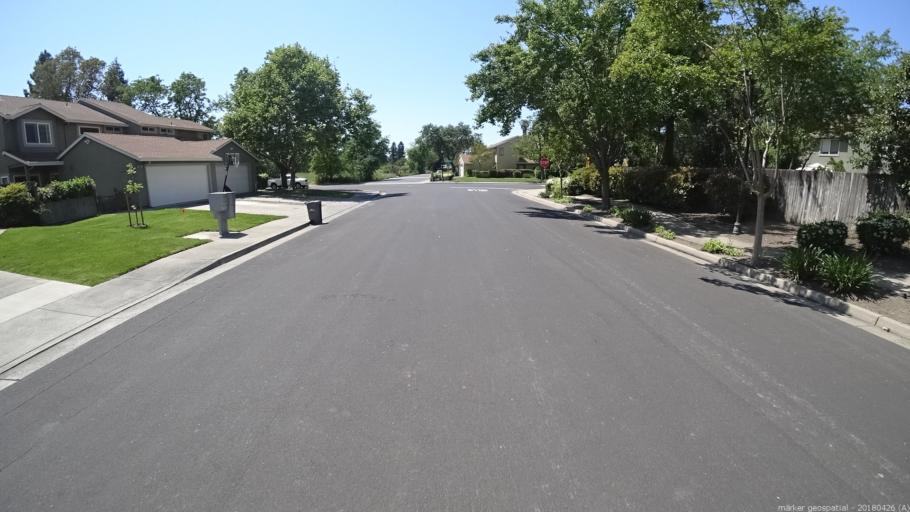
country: US
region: California
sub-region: Yolo County
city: West Sacramento
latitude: 38.5474
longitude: -121.5497
